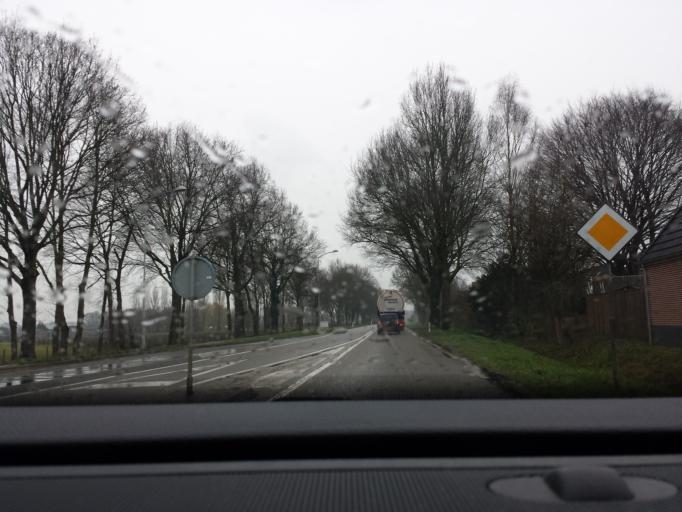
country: NL
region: Gelderland
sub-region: Gemeente Bronckhorst
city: Hengelo
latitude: 52.0451
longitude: 6.3062
